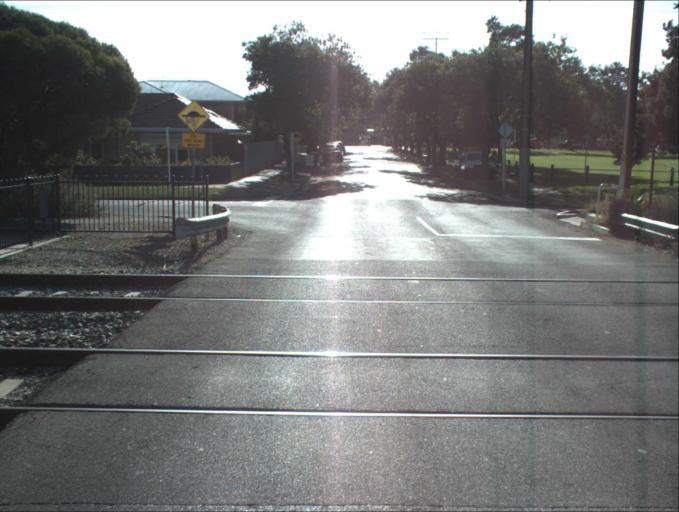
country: AU
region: South Australia
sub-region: Prospect
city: Prospect
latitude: -34.8881
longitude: 138.5834
